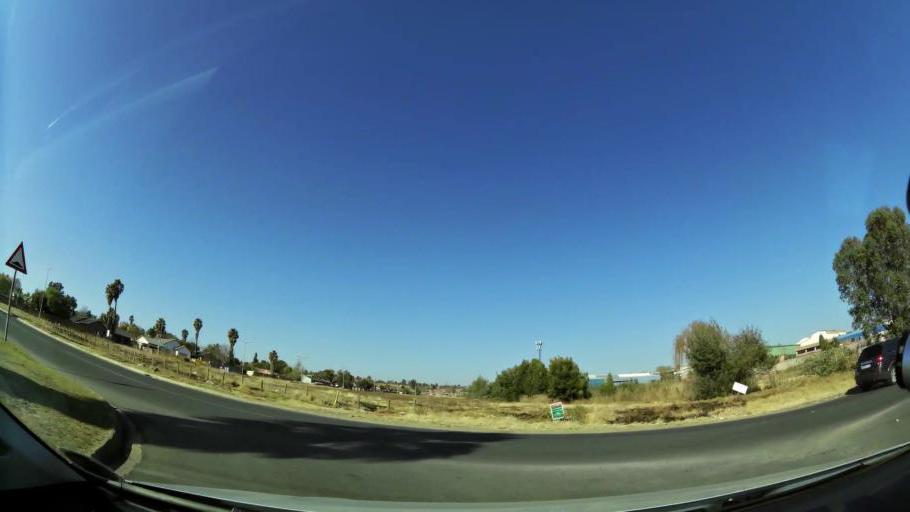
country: ZA
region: Gauteng
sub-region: City of Johannesburg Metropolitan Municipality
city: Modderfontein
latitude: -26.0617
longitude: 28.1983
